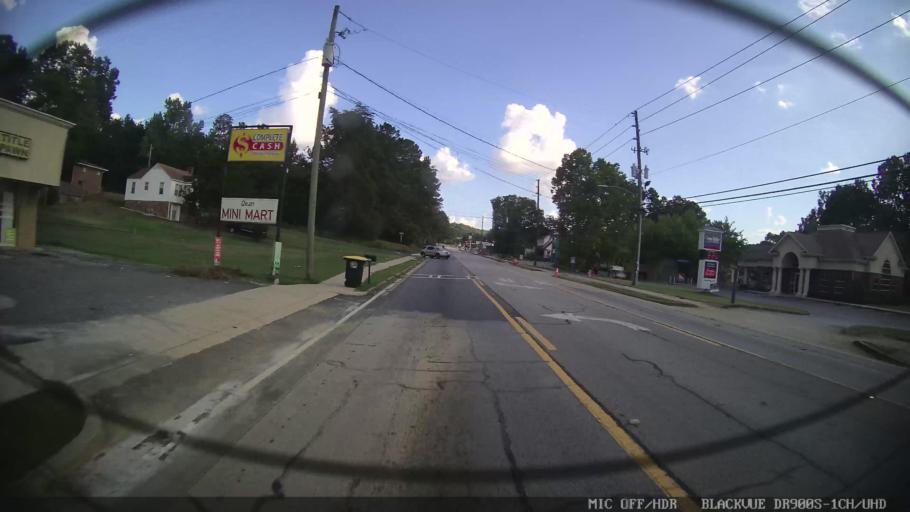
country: US
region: Georgia
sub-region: Floyd County
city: Rome
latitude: 34.2326
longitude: -85.1597
